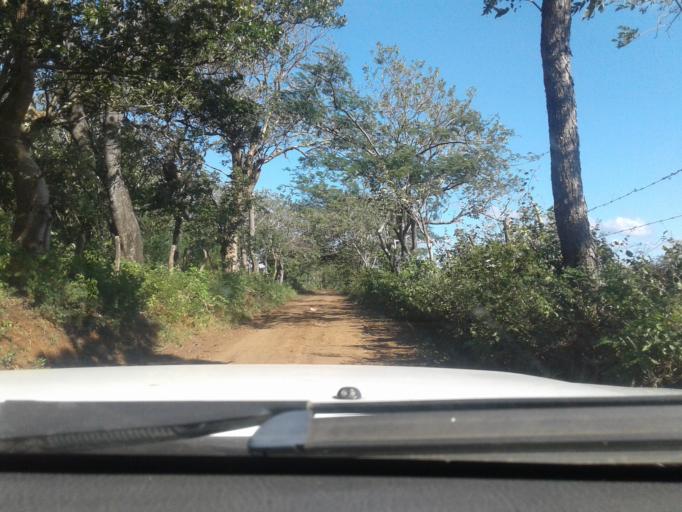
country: NI
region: Carazo
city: Santa Teresa
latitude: 11.7404
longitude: -86.1854
